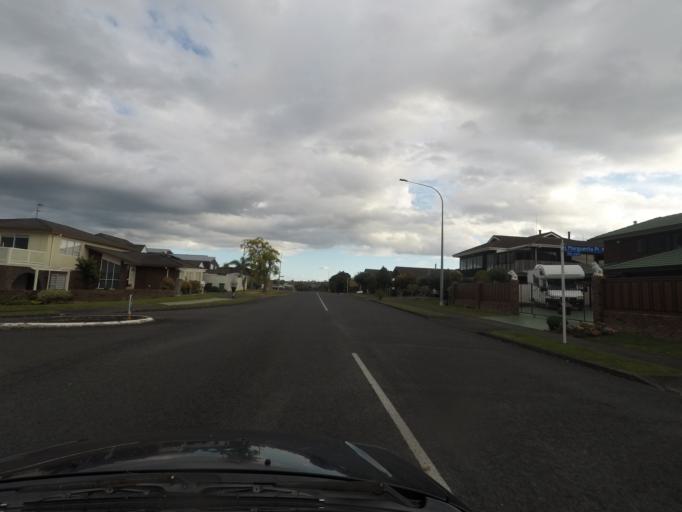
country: NZ
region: Auckland
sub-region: Auckland
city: Rosebank
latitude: -36.8047
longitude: 174.6432
